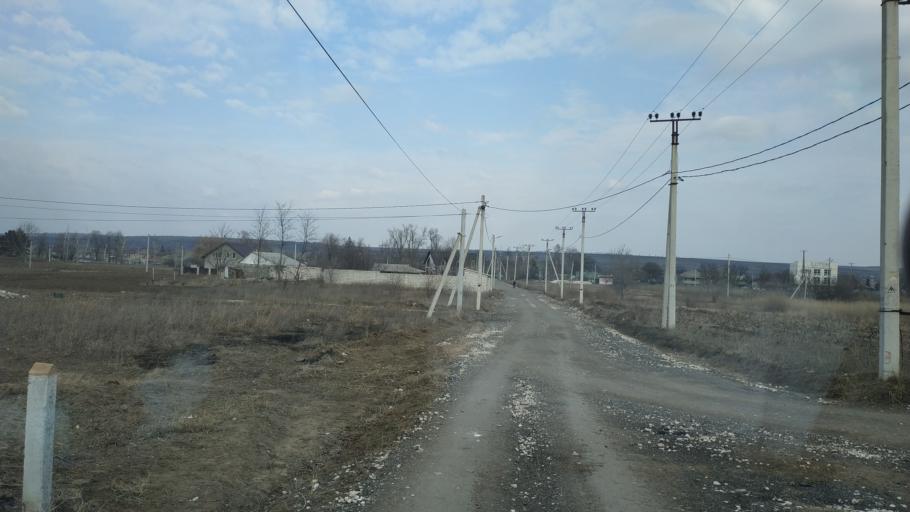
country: MD
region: Anenii Noi
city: Anenii Noi
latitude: 46.8973
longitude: 29.1327
